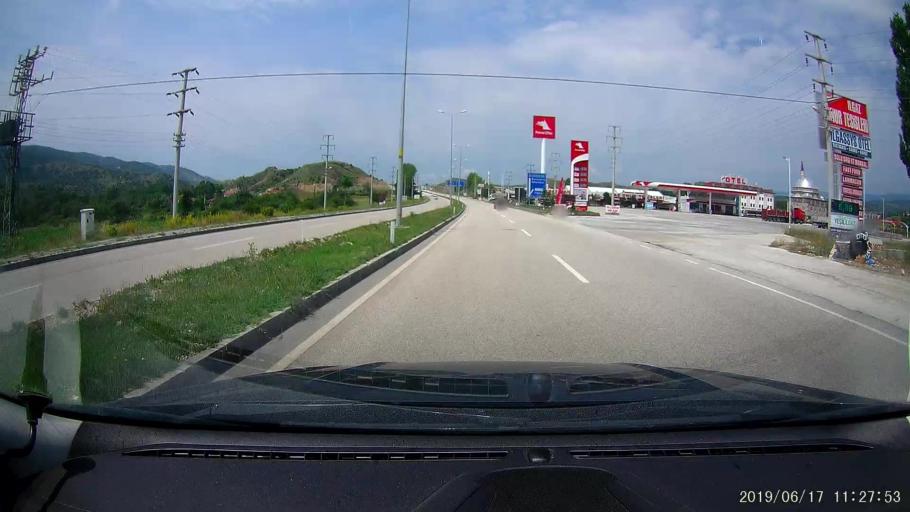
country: TR
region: Cankiri
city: Ilgaz
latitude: 40.9087
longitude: 33.6310
